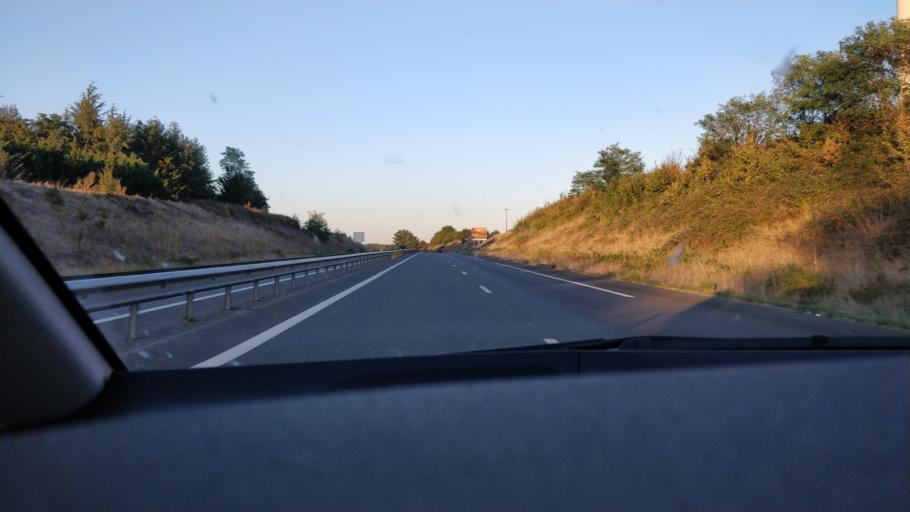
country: FR
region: Poitou-Charentes
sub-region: Departement de la Charente
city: Rivieres
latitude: 45.7417
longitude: 0.3560
